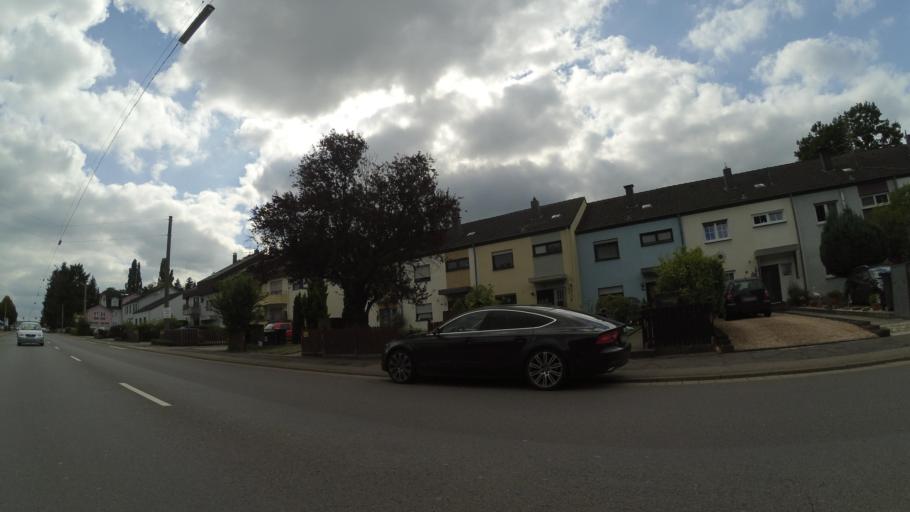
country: DE
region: Saarland
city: Bous
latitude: 49.2618
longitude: 6.8088
